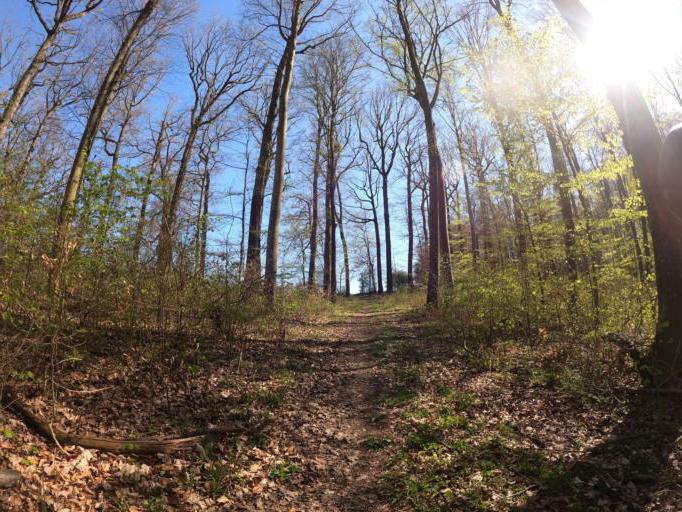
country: DE
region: Baden-Wuerttemberg
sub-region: Karlsruhe Region
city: Monsheim
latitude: 48.9012
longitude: 8.9048
